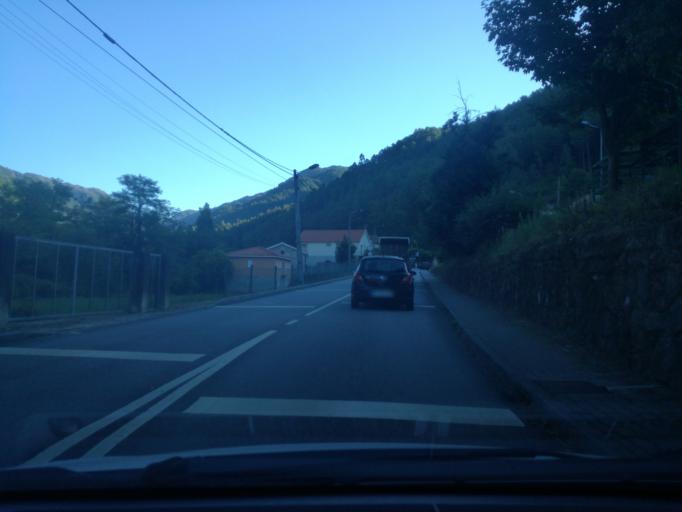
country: PT
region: Braga
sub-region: Vieira do Minho
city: Real
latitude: 41.7160
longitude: -8.1664
